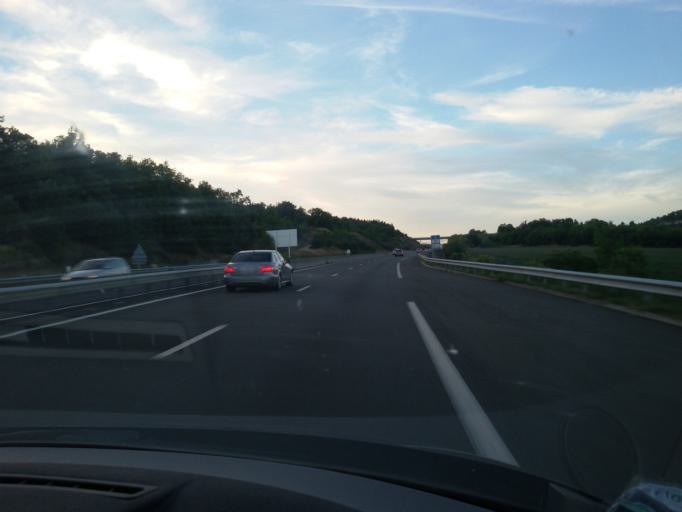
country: FR
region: Languedoc-Roussillon
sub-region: Departement de la Lozere
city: Chirac
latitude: 44.5138
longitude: 3.2413
